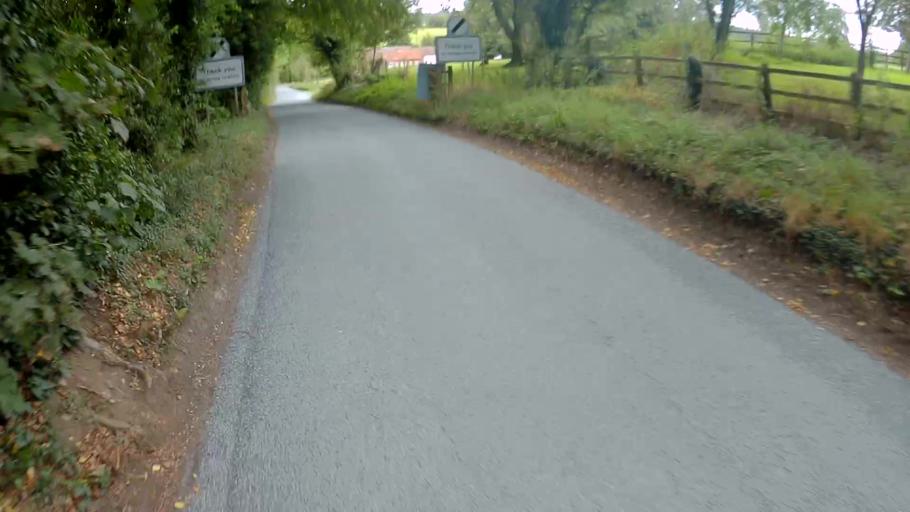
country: GB
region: England
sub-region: Hampshire
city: Overton
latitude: 51.2142
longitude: -1.1997
